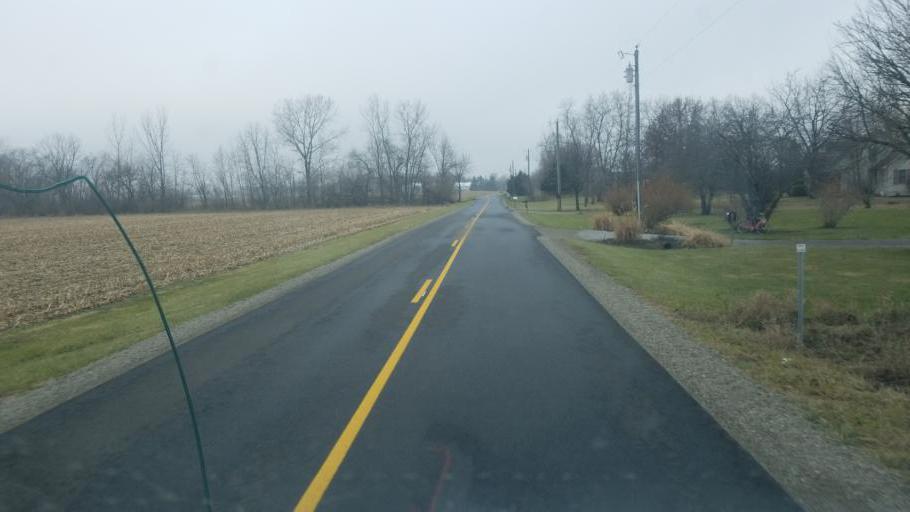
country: US
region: Ohio
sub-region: Champaign County
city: North Lewisburg
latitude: 40.2592
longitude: -83.5508
